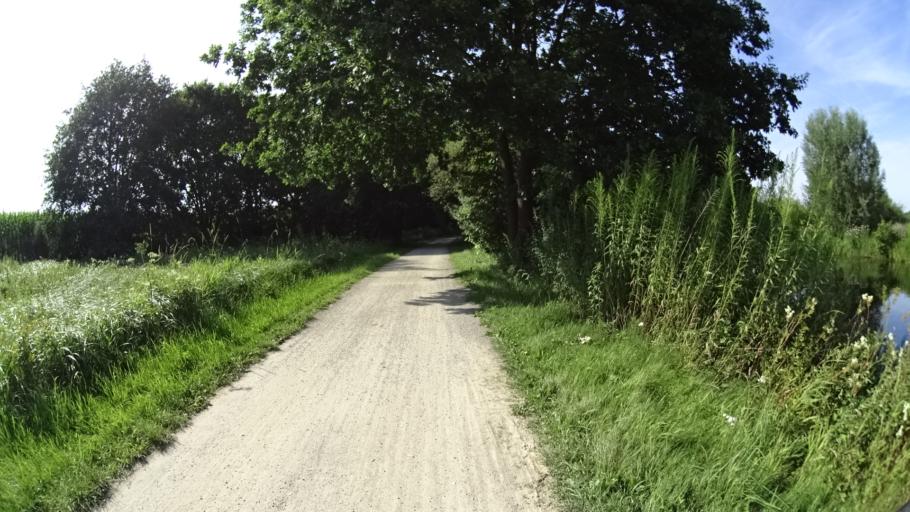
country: DE
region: Lower Saxony
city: Bardowick
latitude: 53.2801
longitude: 10.4103
